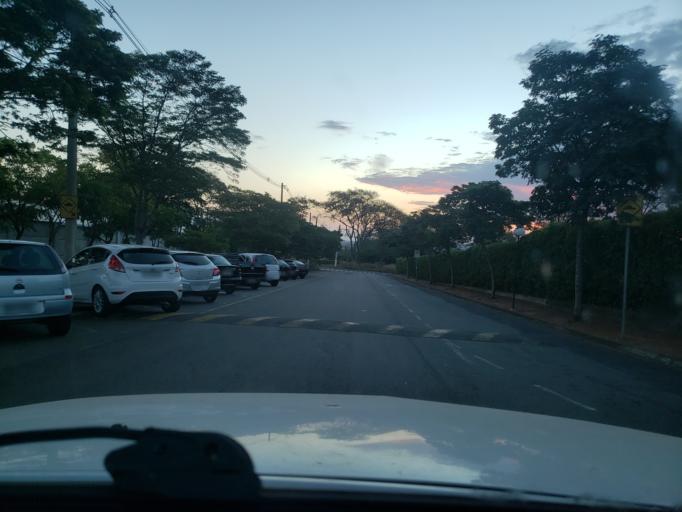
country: BR
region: Sao Paulo
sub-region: Mogi-Mirim
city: Mogi Mirim
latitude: -22.4892
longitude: -46.9797
